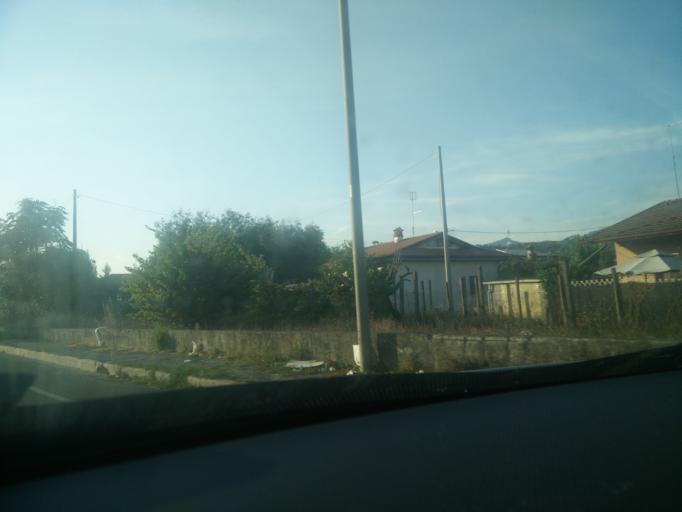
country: IT
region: Tuscany
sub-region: Provincia di Massa-Carrara
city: Massa
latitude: 44.0334
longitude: 10.0931
